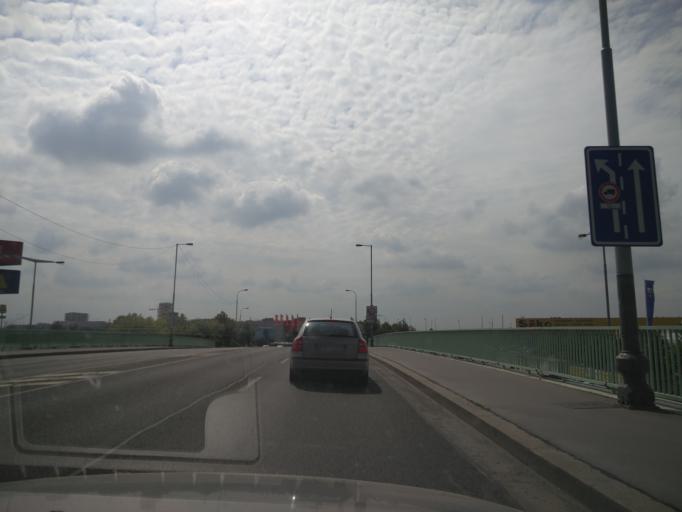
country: CZ
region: Central Bohemia
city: Hostivice
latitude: 50.0518
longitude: 14.2918
